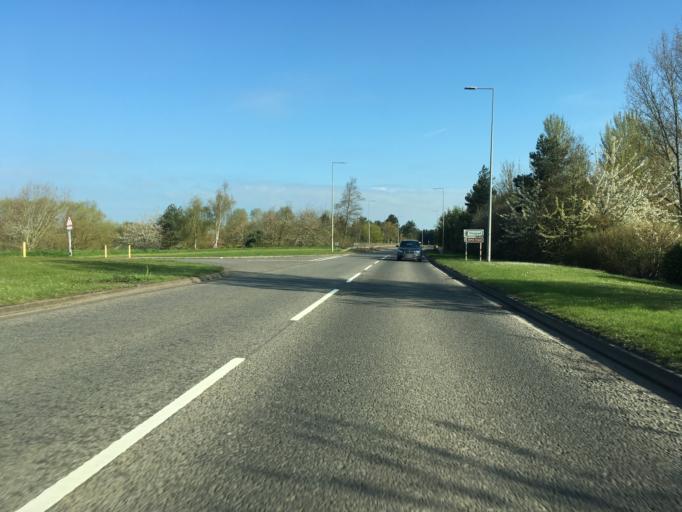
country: GB
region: England
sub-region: Milton Keynes
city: Broughton
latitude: 52.0591
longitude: -0.7138
